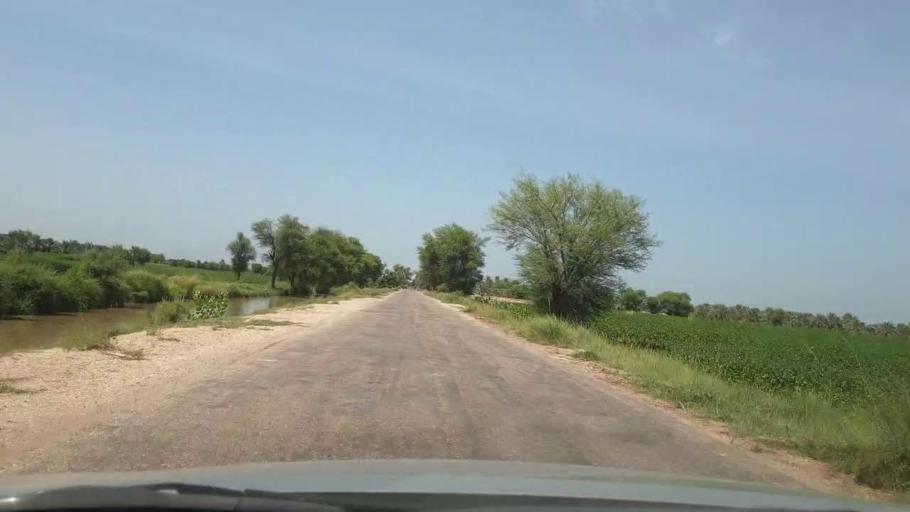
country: PK
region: Sindh
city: Pano Aqil
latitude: 27.6775
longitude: 69.1094
